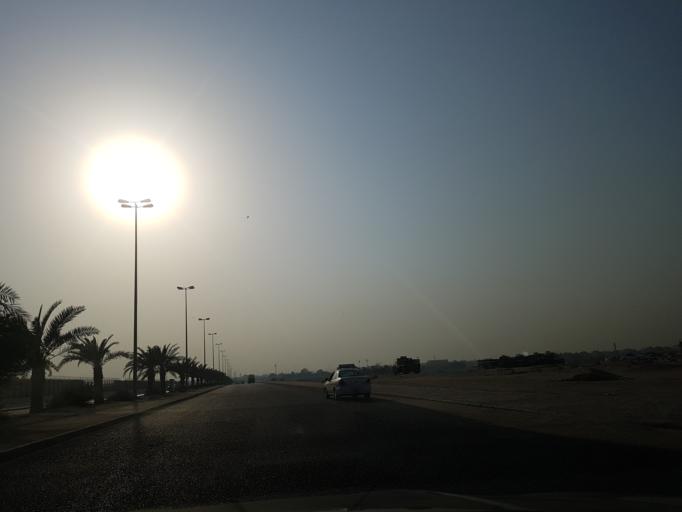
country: KW
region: Al Ahmadi
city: Al Mahbulah
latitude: 29.1209
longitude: 48.1321
